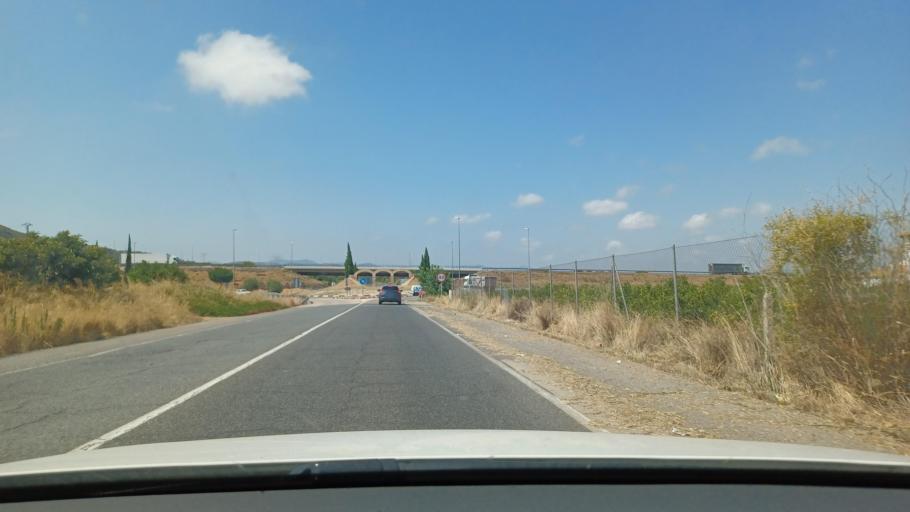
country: ES
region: Valencia
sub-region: Provincia de Valencia
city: Sagunto
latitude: 39.6995
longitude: -0.2612
